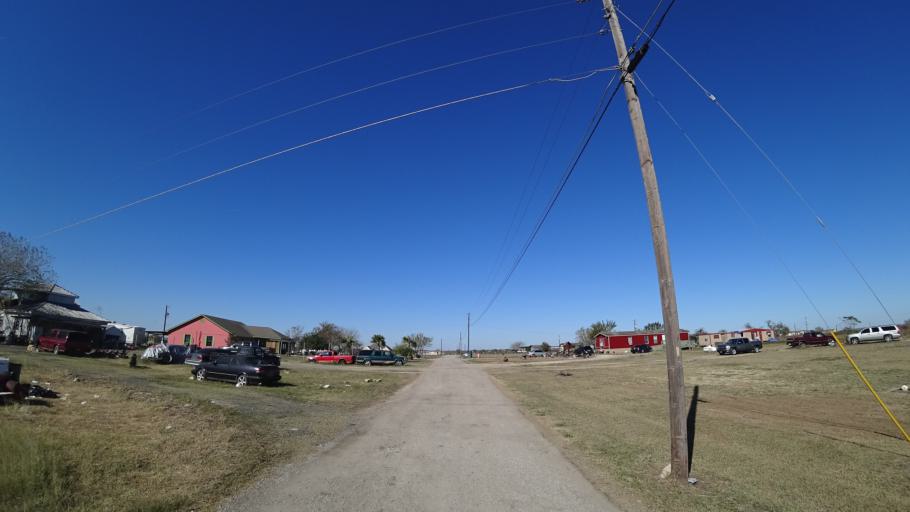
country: US
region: Texas
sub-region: Travis County
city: Garfield
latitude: 30.0994
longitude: -97.6167
